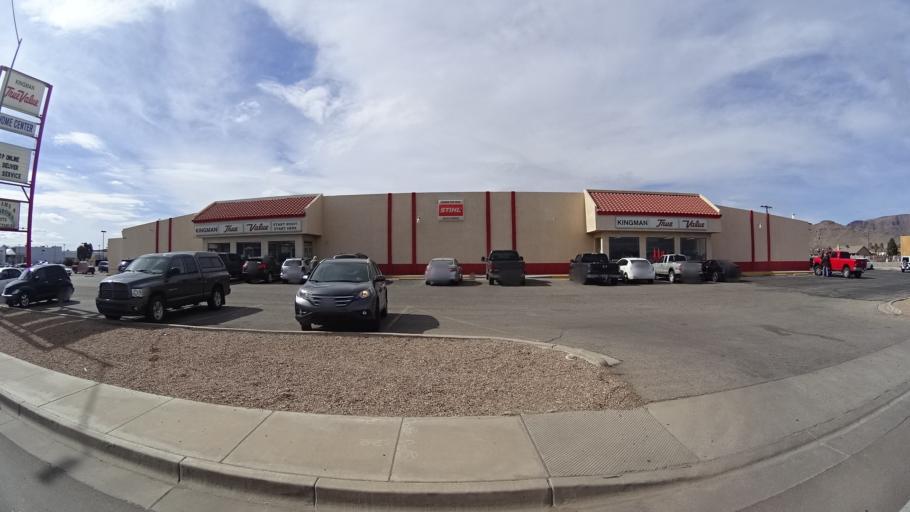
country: US
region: Arizona
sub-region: Mohave County
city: New Kingman-Butler
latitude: 35.2291
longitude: -114.0367
